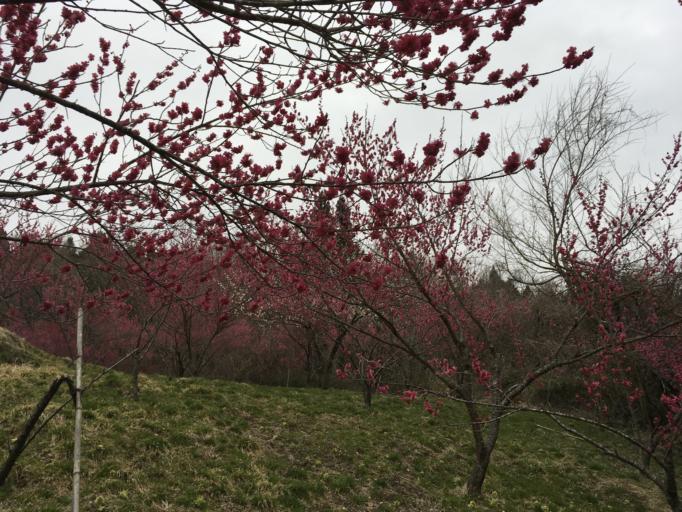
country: JP
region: Iwate
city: Ichinoseki
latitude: 38.7587
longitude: 141.2263
